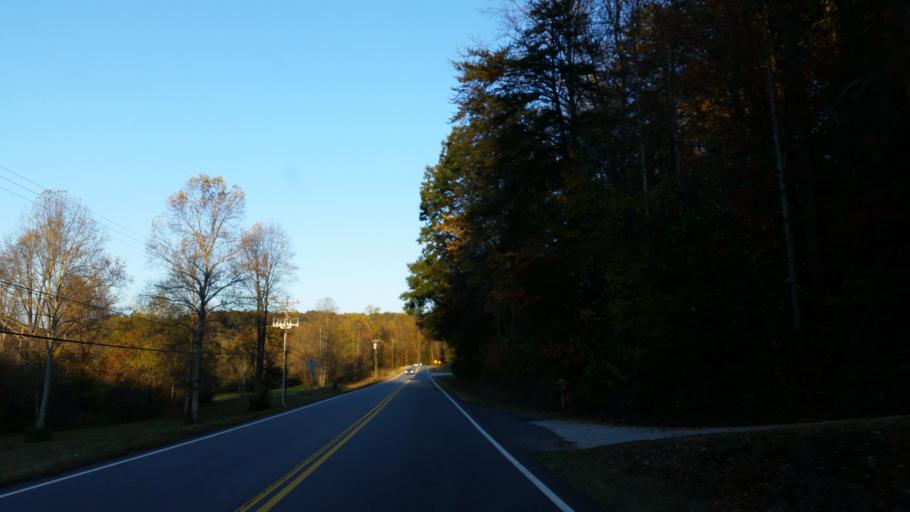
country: US
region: Georgia
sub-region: Lumpkin County
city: Dahlonega
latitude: 34.5313
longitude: -84.0135
